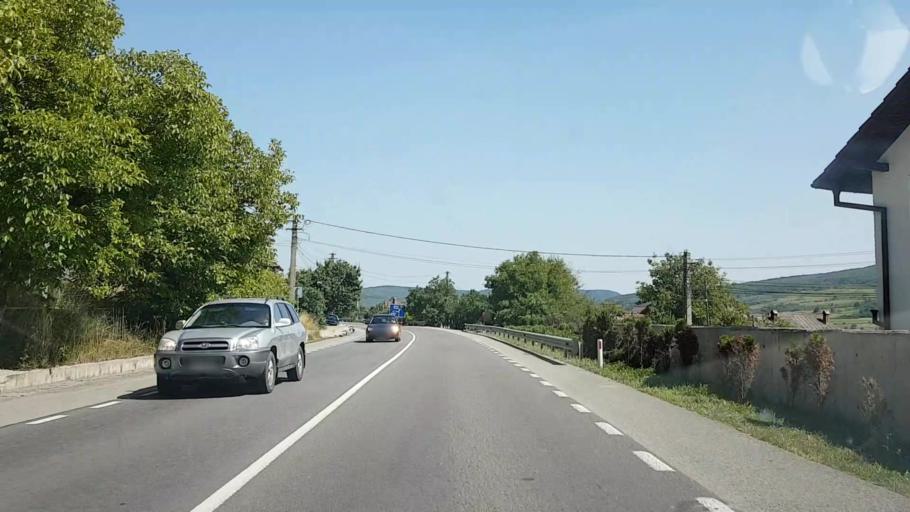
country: RO
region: Bistrita-Nasaud
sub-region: Comuna Beclean
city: Beclean
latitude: 47.1806
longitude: 24.1399
